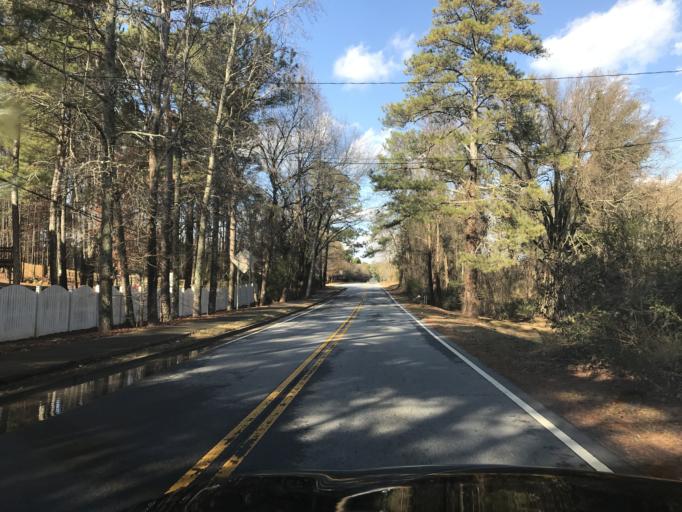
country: US
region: Georgia
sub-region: Cobb County
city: Mableton
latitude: 33.7134
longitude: -84.5593
